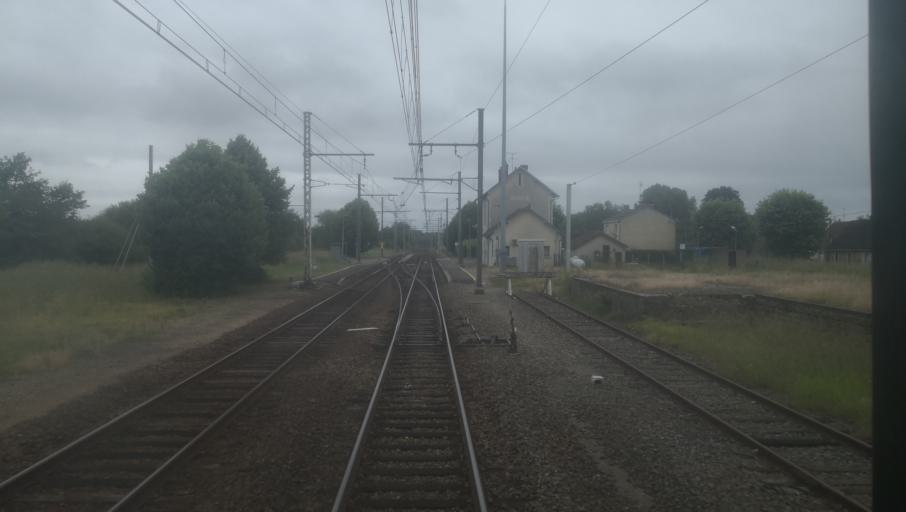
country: FR
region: Centre
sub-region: Departement de l'Indre
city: Chantome
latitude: 46.4397
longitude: 1.5523
